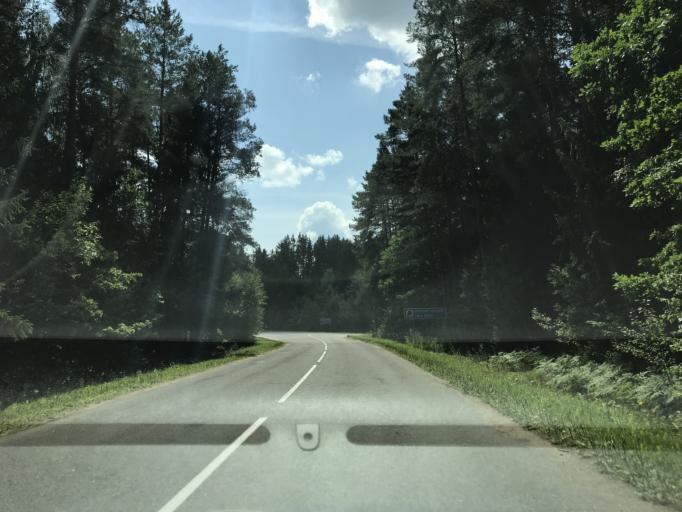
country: BY
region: Minsk
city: Rakaw
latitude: 53.9871
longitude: 26.9901
